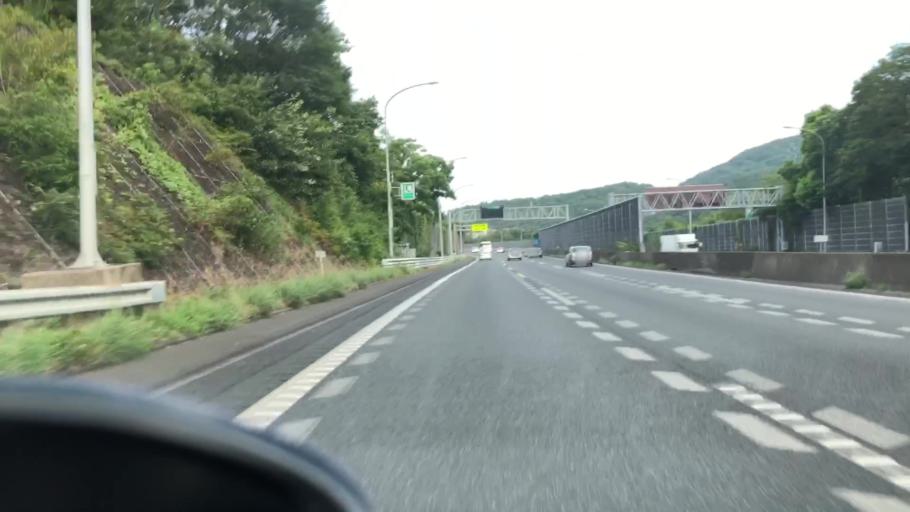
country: JP
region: Hyogo
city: Takarazuka
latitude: 34.8237
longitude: 135.3147
